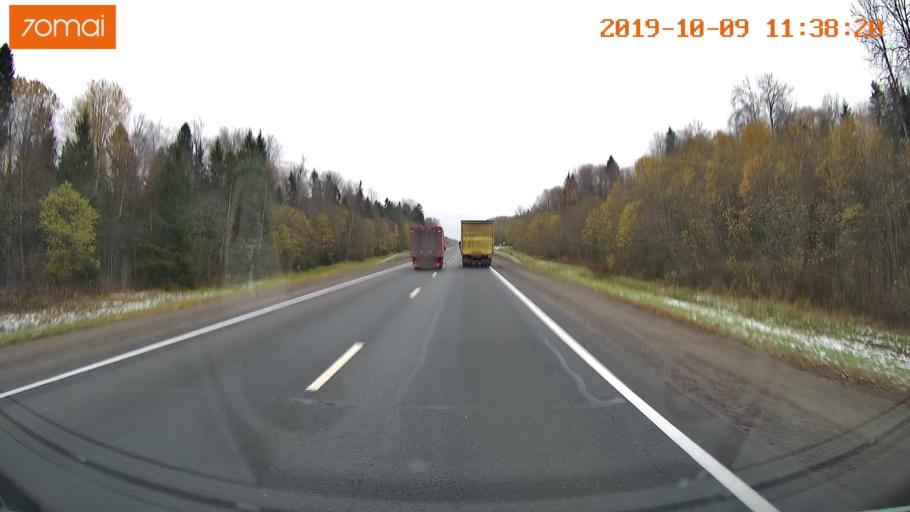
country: RU
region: Vologda
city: Gryazovets
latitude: 58.9693
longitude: 40.1548
